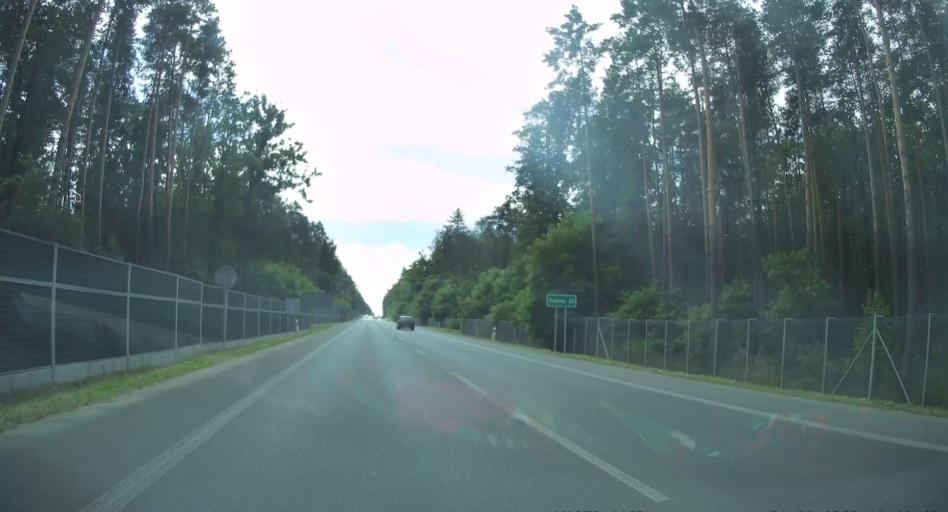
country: PL
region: Subcarpathian Voivodeship
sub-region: Powiat mielecki
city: Mielec
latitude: 50.2765
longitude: 21.4973
